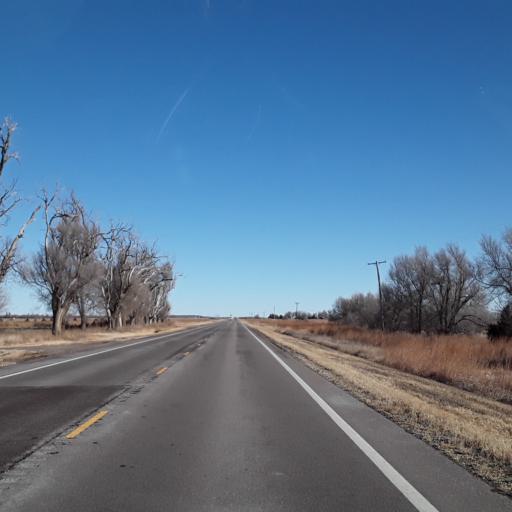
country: US
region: Kansas
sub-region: Pawnee County
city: Larned
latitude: 38.1244
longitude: -99.1728
